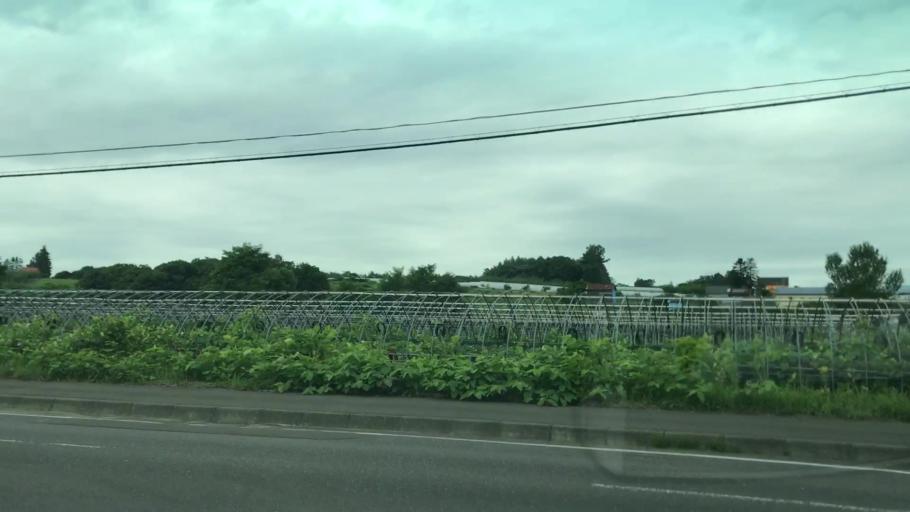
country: JP
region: Hokkaido
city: Yoichi
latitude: 43.1766
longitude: 140.8218
